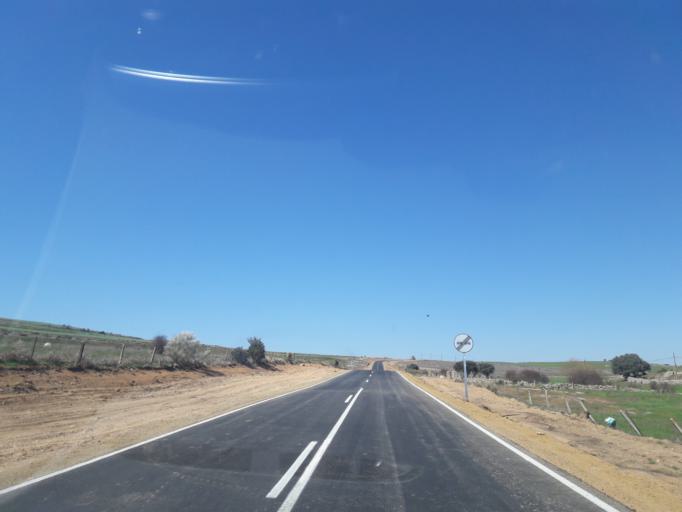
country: ES
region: Castille and Leon
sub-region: Provincia de Salamanca
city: Valdemierque
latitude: 40.8229
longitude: -5.5653
